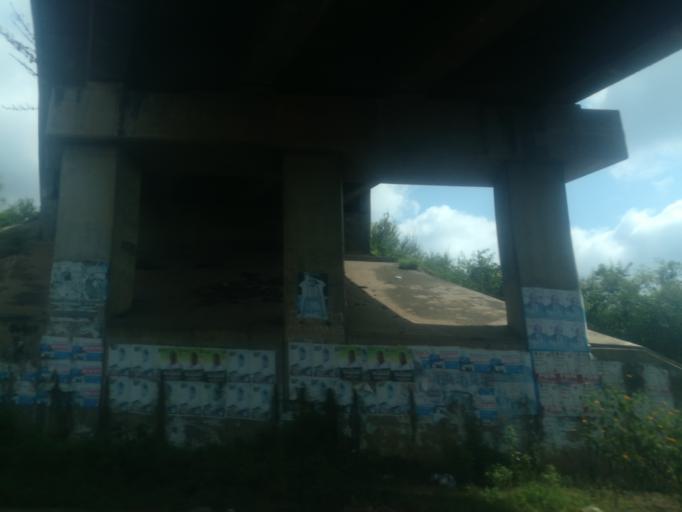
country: NG
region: Oyo
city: Moniya
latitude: 7.5887
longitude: 3.9139
